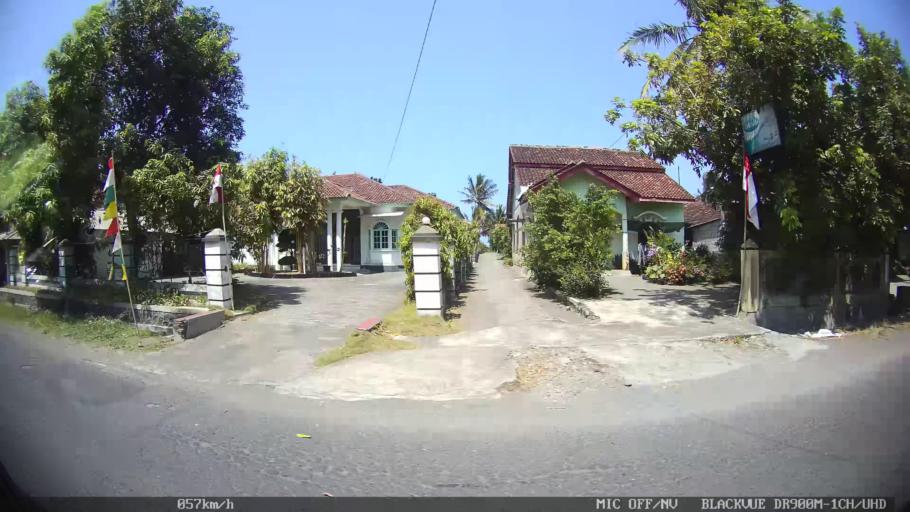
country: ID
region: Daerah Istimewa Yogyakarta
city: Srandakan
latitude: -7.9112
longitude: 110.0893
